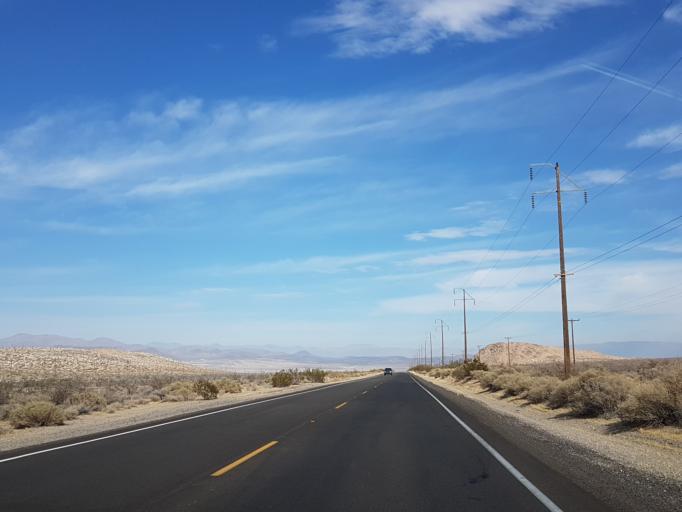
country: US
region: California
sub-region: Kern County
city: Ridgecrest
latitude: 35.6269
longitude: -117.5894
